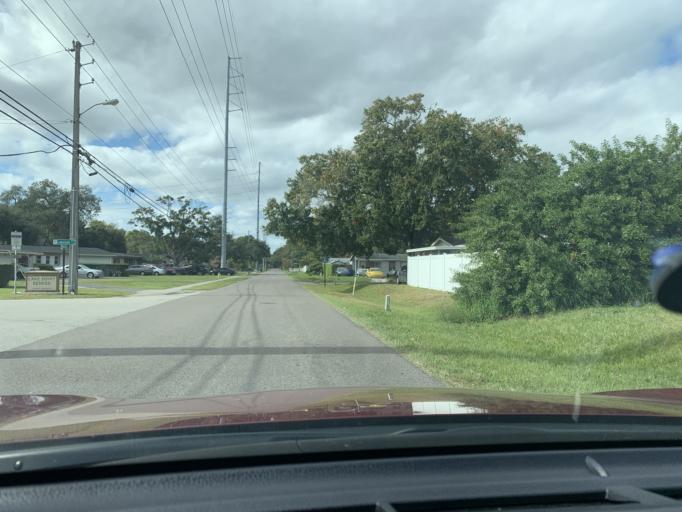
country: US
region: Florida
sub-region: Hillsborough County
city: Egypt Lake-Leto
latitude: 28.0181
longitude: -82.4948
